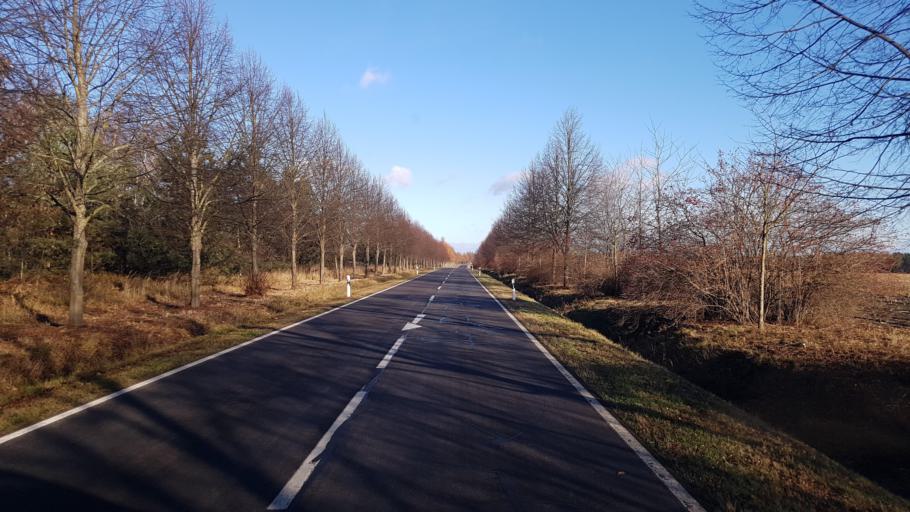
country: DE
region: Brandenburg
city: Forst
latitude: 51.7594
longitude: 14.5656
